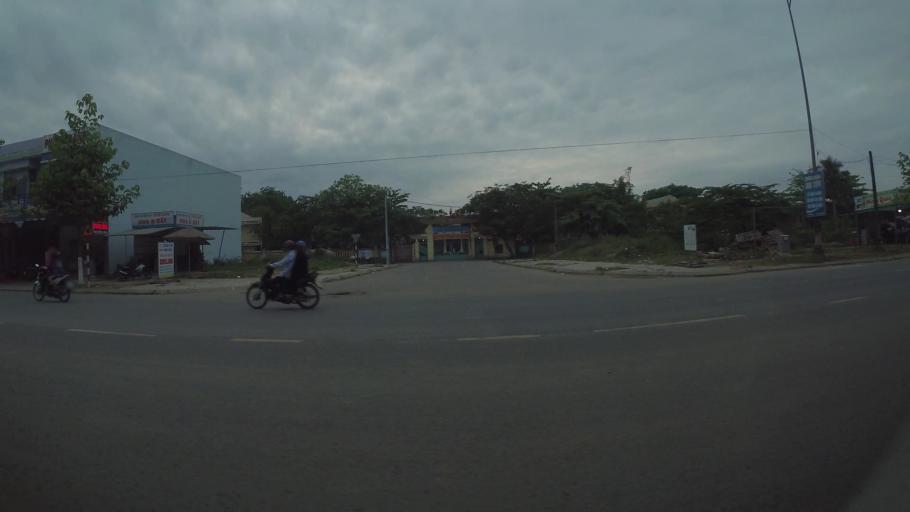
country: VN
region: Da Nang
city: Lien Chieu
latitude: 16.0728
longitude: 108.1103
